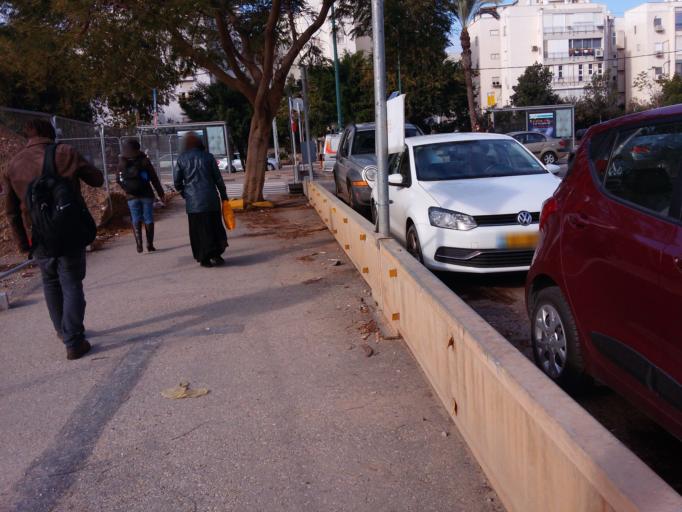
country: IL
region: Tel Aviv
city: Tel Aviv
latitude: 32.0837
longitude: 34.7947
